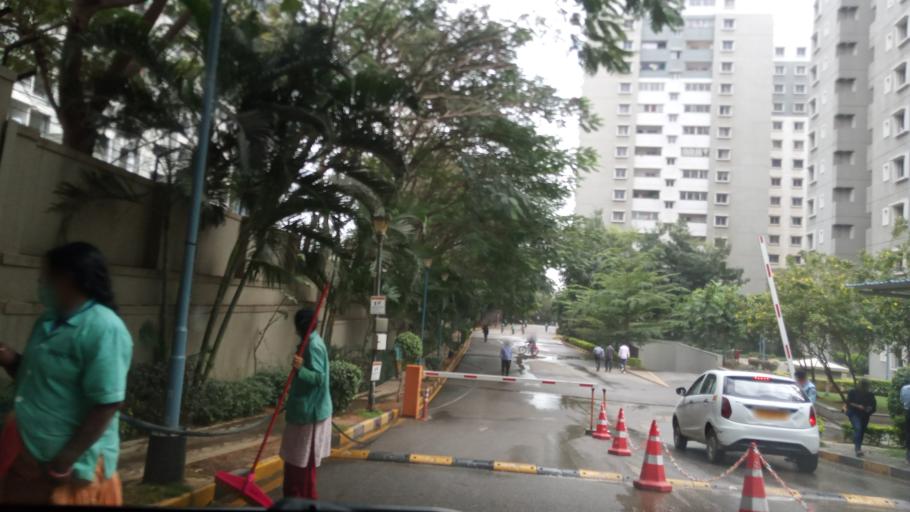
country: IN
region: Karnataka
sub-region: Bangalore Urban
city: Yelahanka
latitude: 13.0461
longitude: 77.5013
